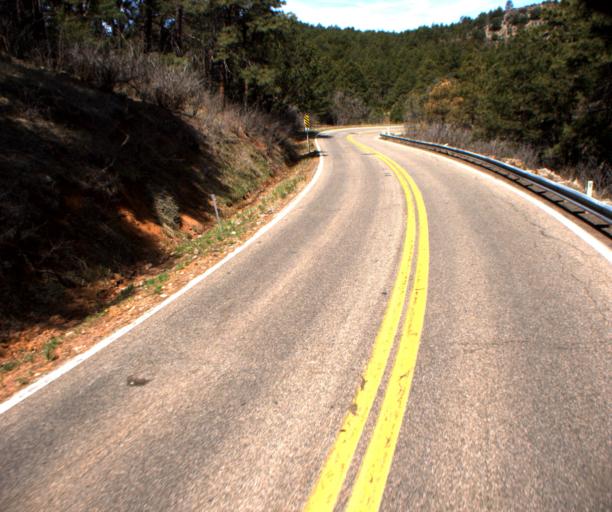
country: US
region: Arizona
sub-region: Yavapai County
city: Clarkdale
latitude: 34.7103
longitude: -112.1506
